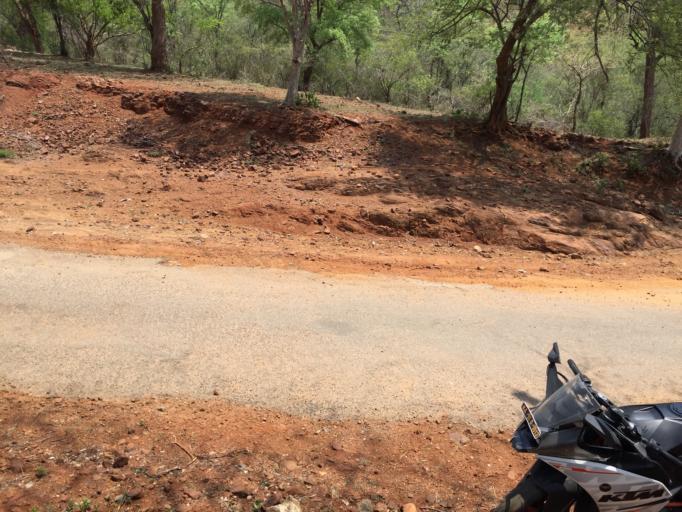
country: IN
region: Karnataka
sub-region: Chamrajnagar
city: Kollegal
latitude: 12.3007
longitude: 77.3030
